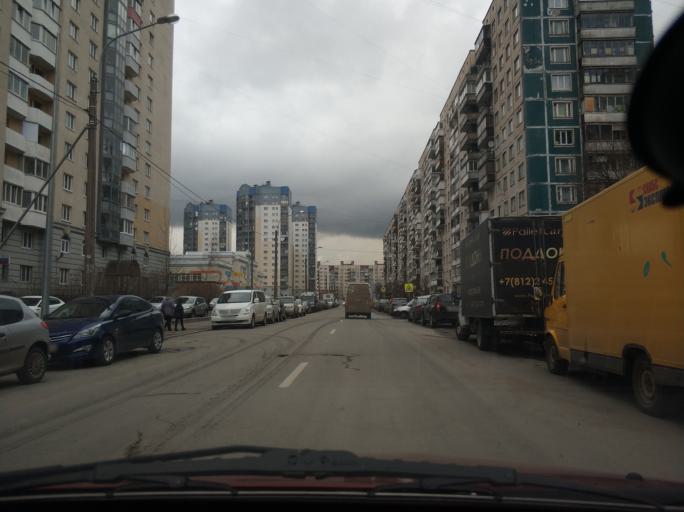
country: RU
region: St.-Petersburg
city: Krasnogvargeisky
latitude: 59.9464
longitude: 30.4841
